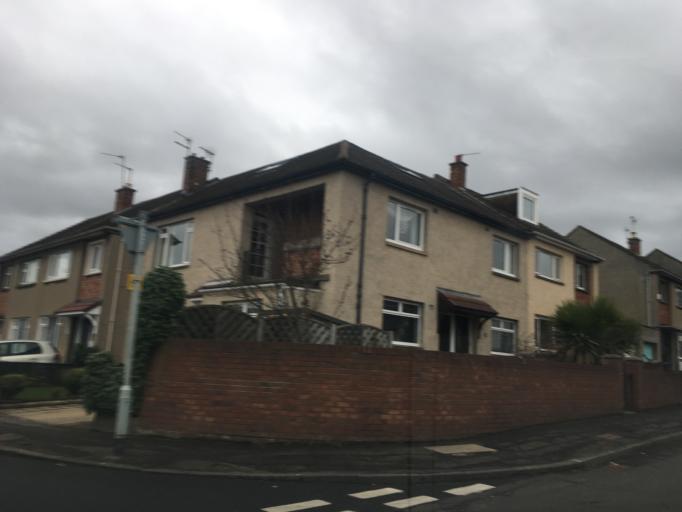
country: GB
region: Scotland
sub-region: Edinburgh
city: Colinton
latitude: 55.9090
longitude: -3.2172
